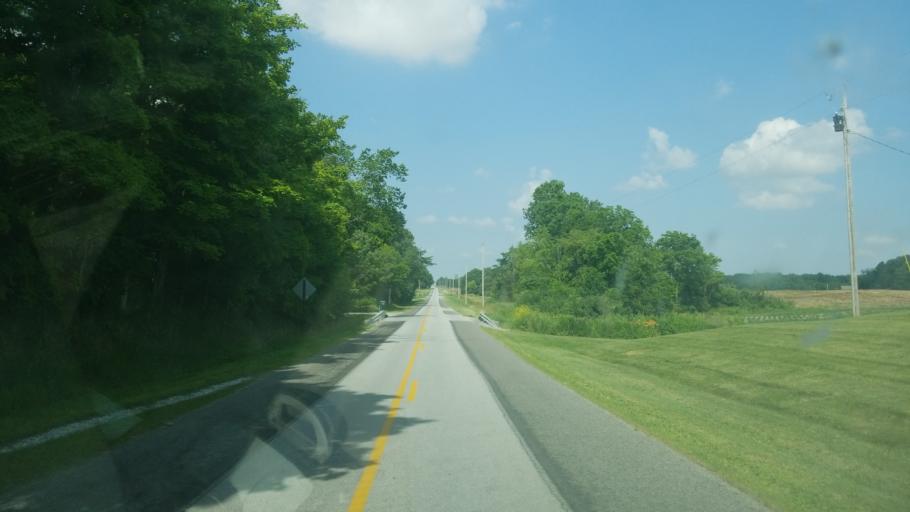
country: US
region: Ohio
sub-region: Auglaize County
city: Cridersville
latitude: 40.5713
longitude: -84.0631
